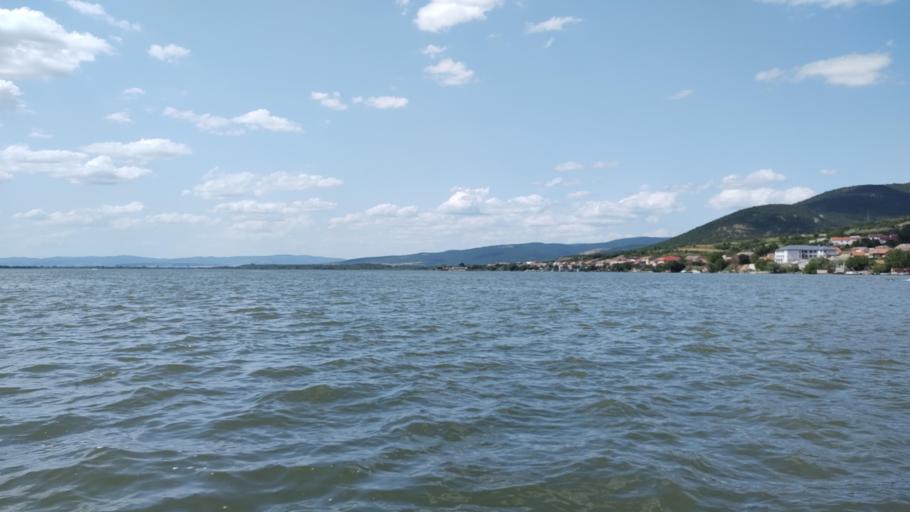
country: RO
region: Caras-Severin
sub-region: Comuna Pescari
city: Coronini
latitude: 44.6744
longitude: 21.6778
